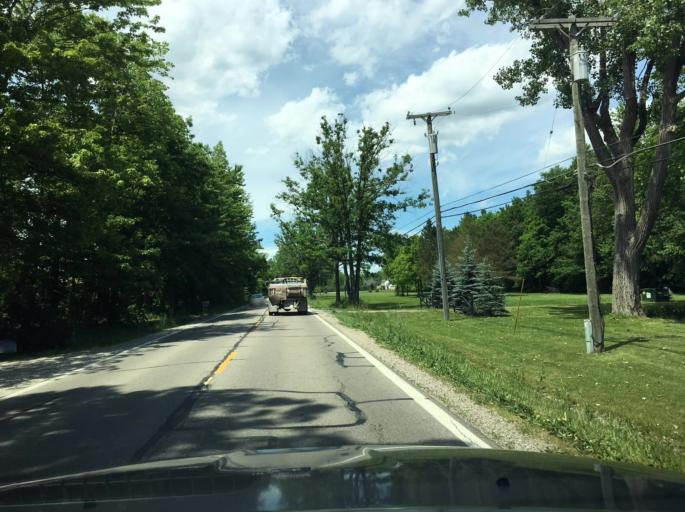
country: US
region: Michigan
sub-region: Macomb County
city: Romeo
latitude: 42.7526
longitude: -82.9608
